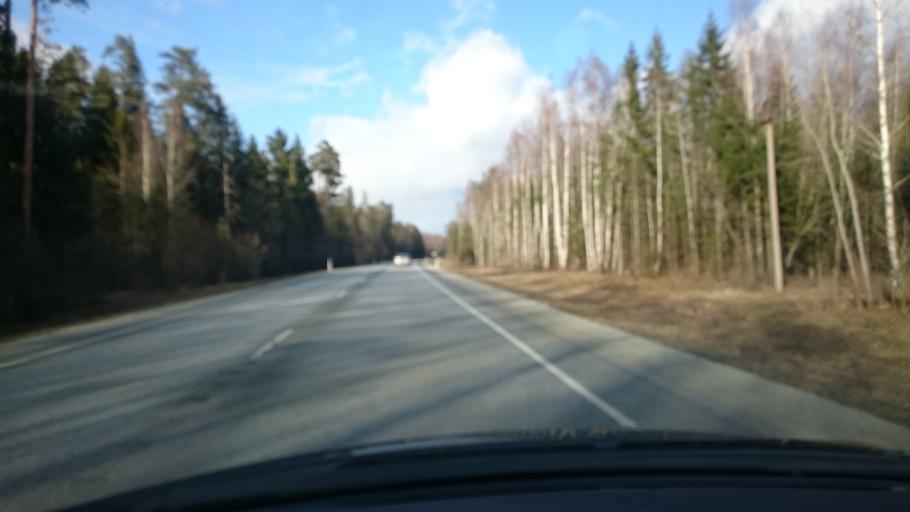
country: EE
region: Harju
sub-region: Keila linn
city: Keila
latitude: 59.1919
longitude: 24.4027
